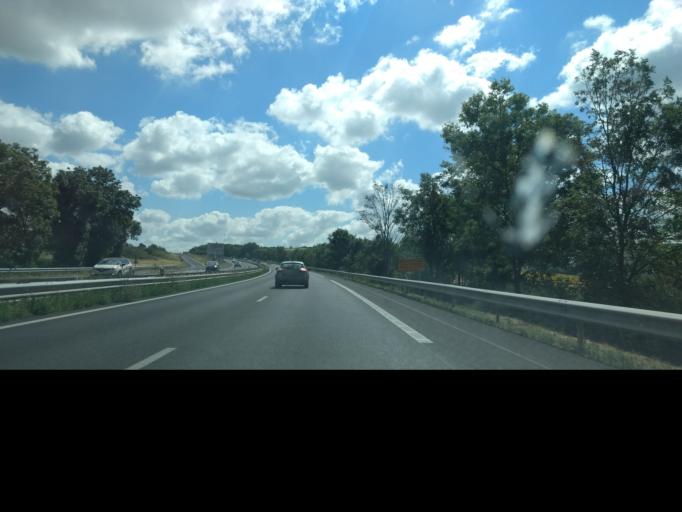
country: FR
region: Auvergne
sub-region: Departement du Puy-de-Dome
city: Aulnat
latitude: 45.7715
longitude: 3.1510
